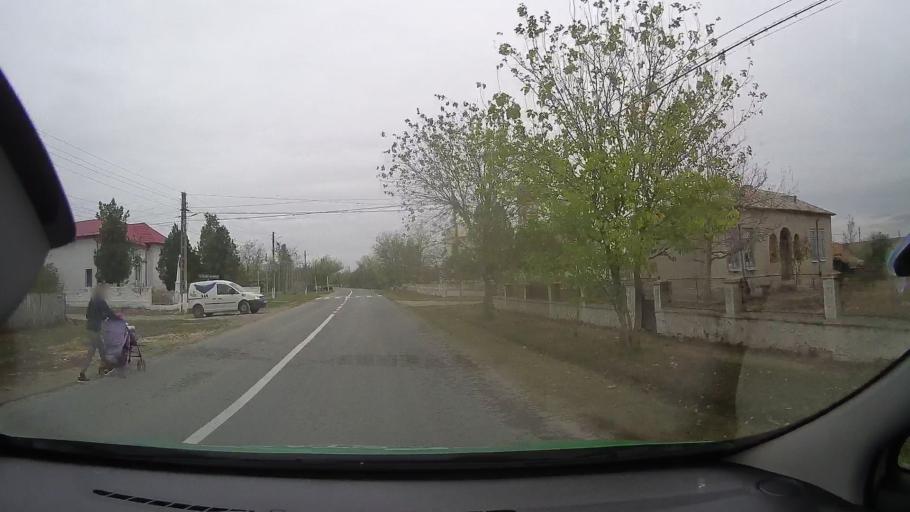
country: RO
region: Constanta
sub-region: Comuna Silistea
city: Silistea
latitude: 44.4458
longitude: 28.2383
